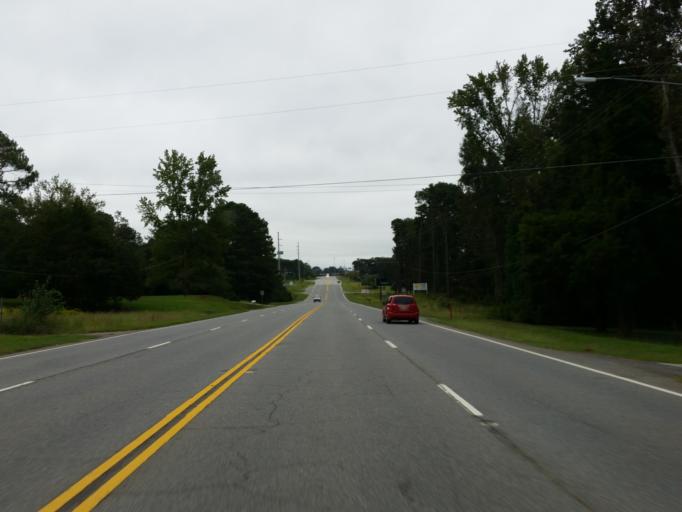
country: US
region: Georgia
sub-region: Houston County
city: Perry
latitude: 32.4787
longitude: -83.7536
